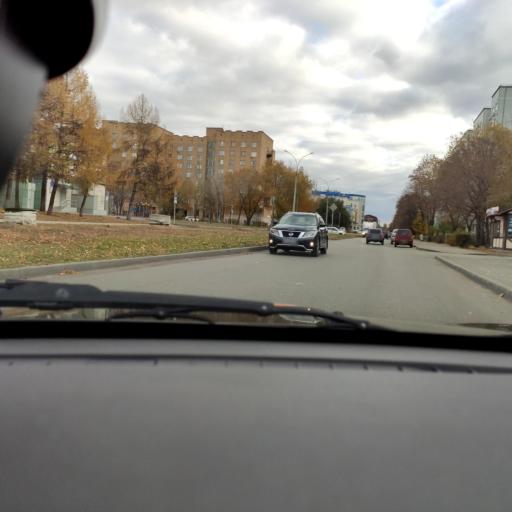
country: RU
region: Samara
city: Tol'yatti
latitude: 53.5335
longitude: 49.3141
